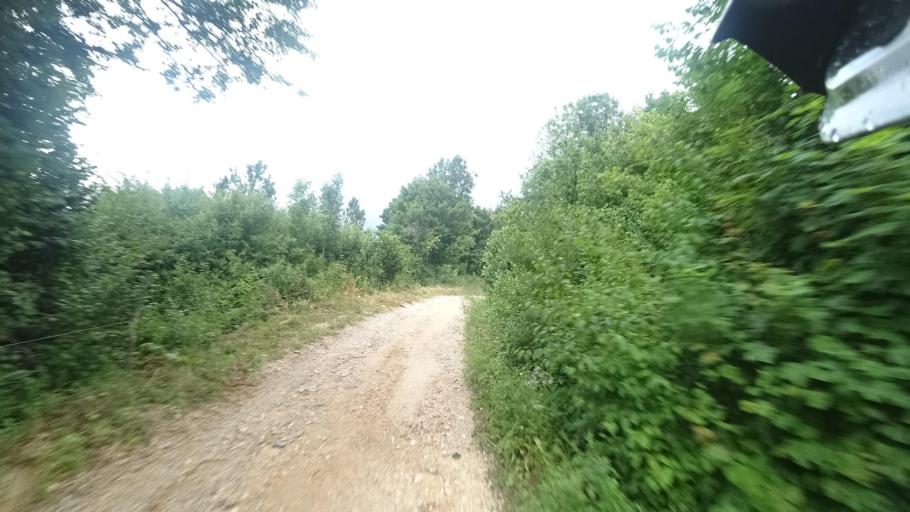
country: HR
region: Licko-Senjska
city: Jezerce
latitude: 44.7611
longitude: 15.6360
